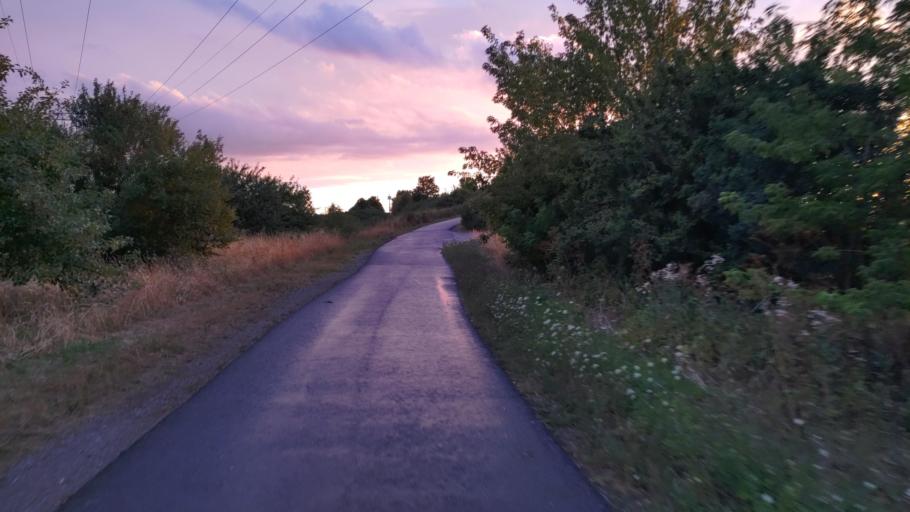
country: DE
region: Thuringia
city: Kleinmolsen
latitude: 50.9890
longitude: 11.0883
